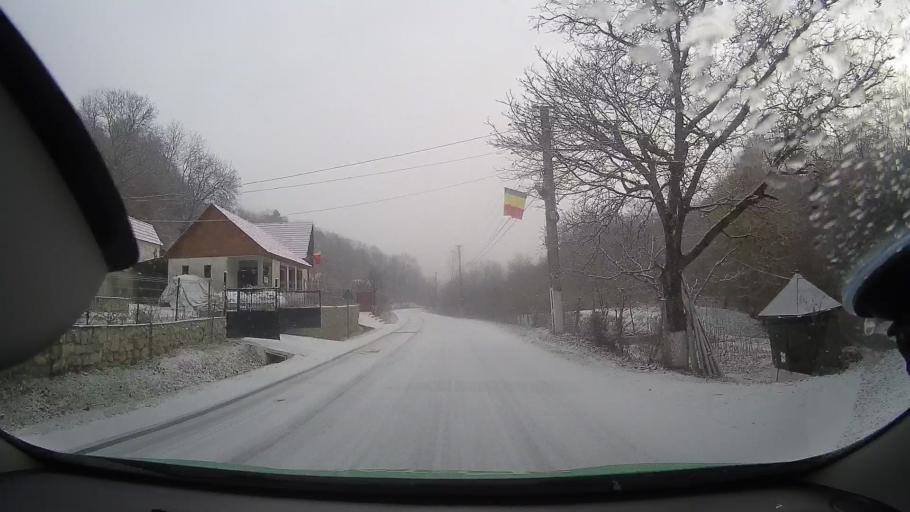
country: RO
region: Alba
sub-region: Comuna Livezile
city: Livezile
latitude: 46.3664
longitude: 23.5948
